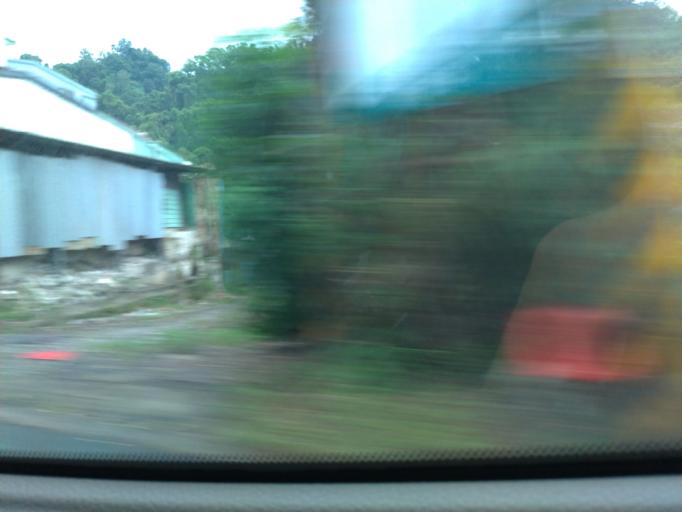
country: TW
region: Taipei
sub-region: Taipei
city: Banqiao
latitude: 24.9282
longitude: 121.4240
